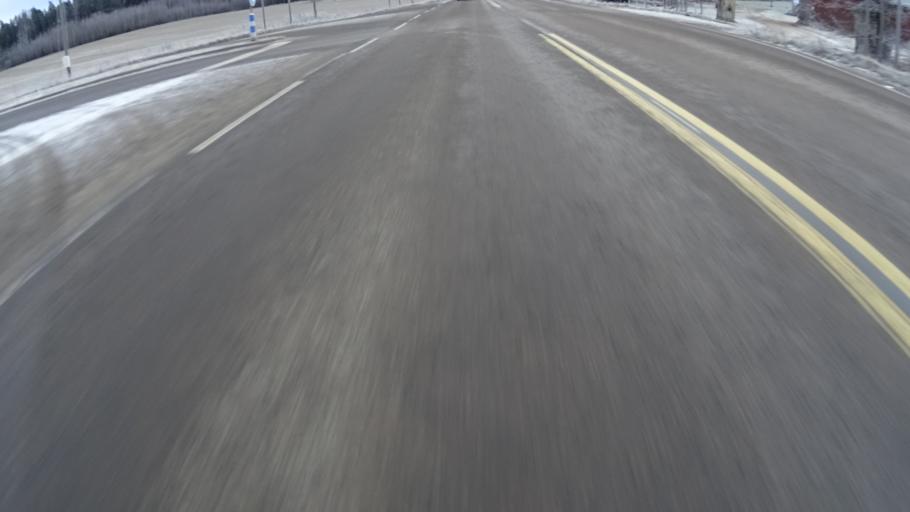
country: FI
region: Uusimaa
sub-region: Helsinki
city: Nurmijaervi
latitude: 60.4302
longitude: 24.7225
